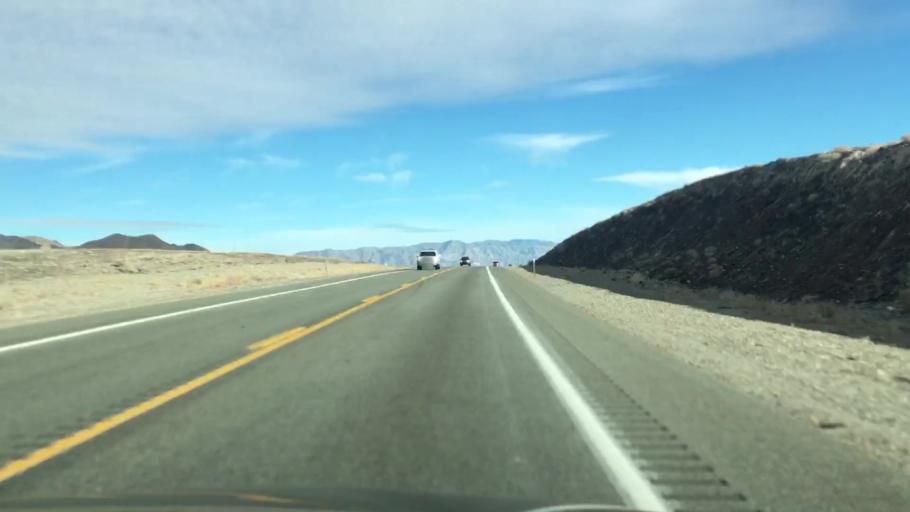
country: US
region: Nevada
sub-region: Mineral County
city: Hawthorne
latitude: 38.5497
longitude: -118.4371
